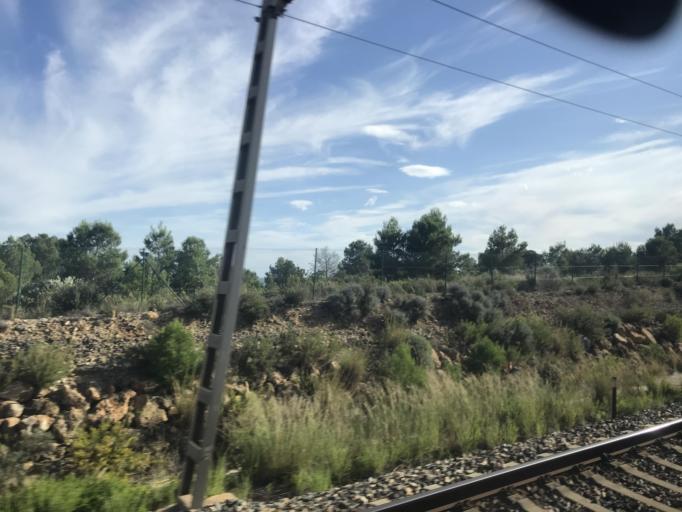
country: ES
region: Catalonia
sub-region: Provincia de Tarragona
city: El Perello
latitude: 40.8526
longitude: 0.7621
